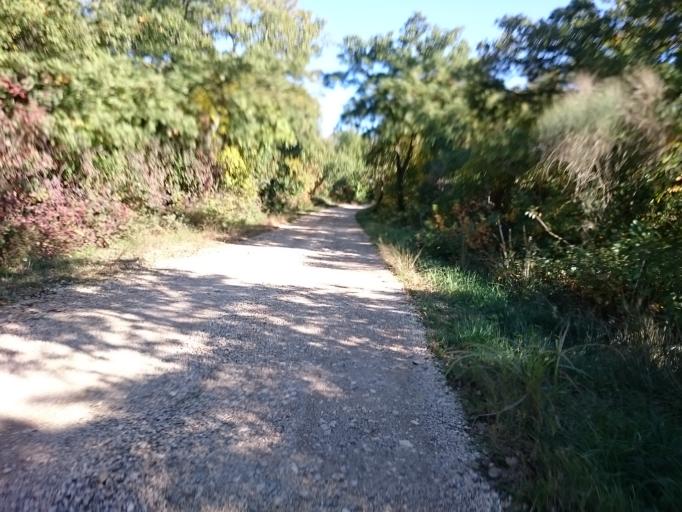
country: HR
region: Istarska
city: Umag
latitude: 45.4645
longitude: 13.5599
